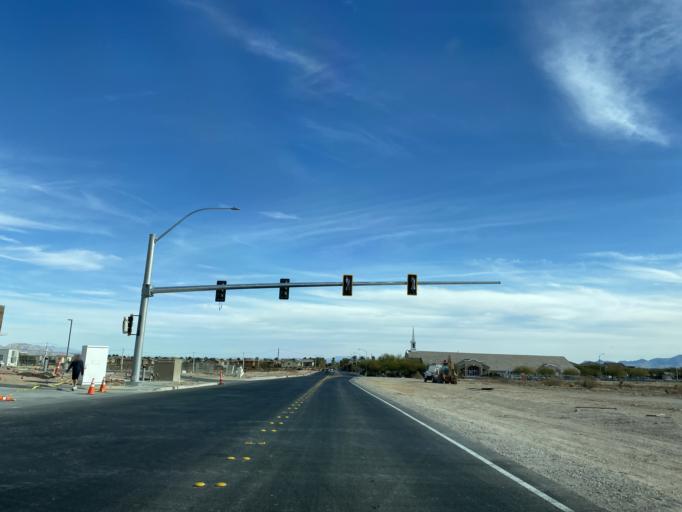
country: US
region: Nevada
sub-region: Clark County
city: Enterprise
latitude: 36.0483
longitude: -115.2655
